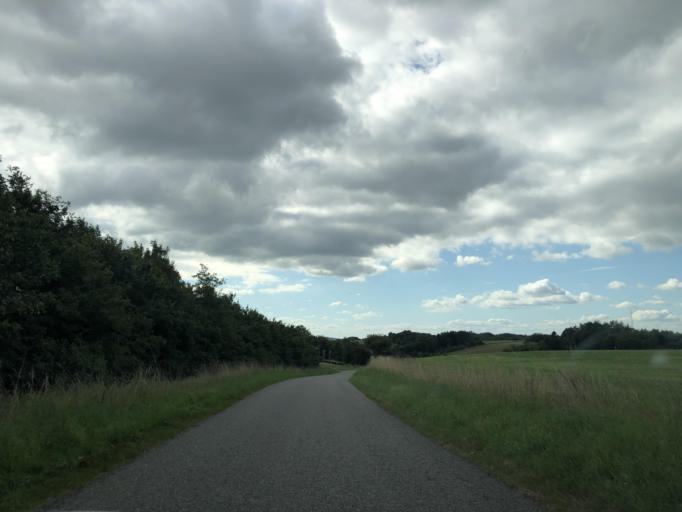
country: DK
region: North Denmark
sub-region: Vesthimmerland Kommune
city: Alestrup
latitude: 56.5907
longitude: 9.4046
